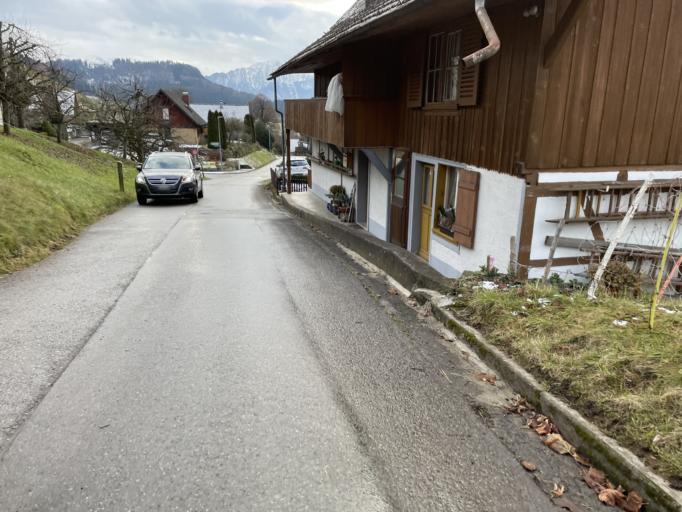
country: CH
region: Lucerne
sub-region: Entlebuch District
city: Oberdiessbach
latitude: 46.8249
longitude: 7.6148
